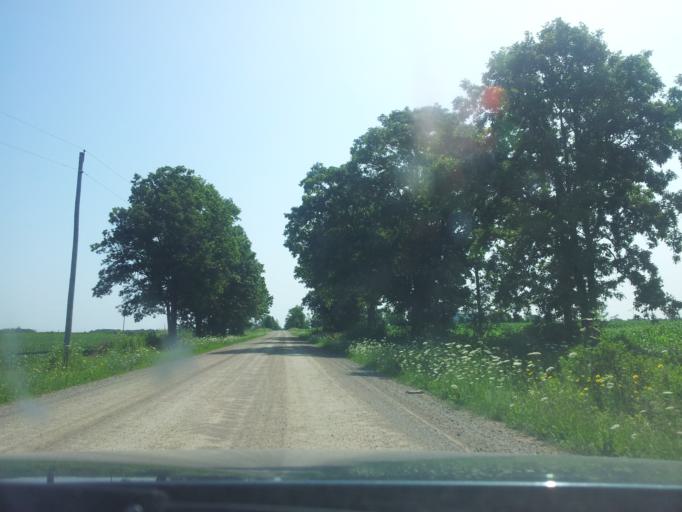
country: CA
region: Ontario
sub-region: Oxford County
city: Woodstock
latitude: 42.9545
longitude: -80.6171
